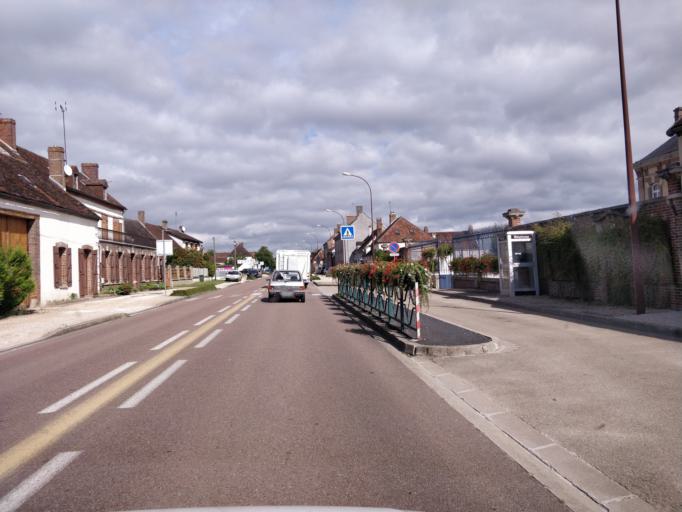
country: FR
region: Champagne-Ardenne
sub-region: Departement de l'Aube
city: Aix-en-Othe
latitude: 48.2349
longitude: 3.6680
